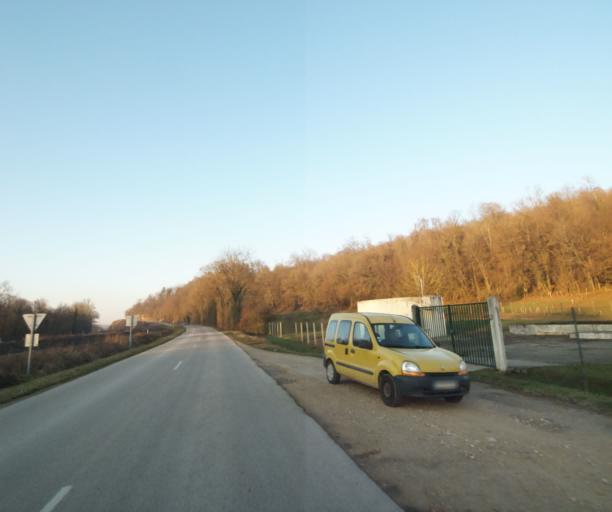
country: FR
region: Champagne-Ardenne
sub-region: Departement de la Haute-Marne
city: Bienville
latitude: 48.5847
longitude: 5.0450
